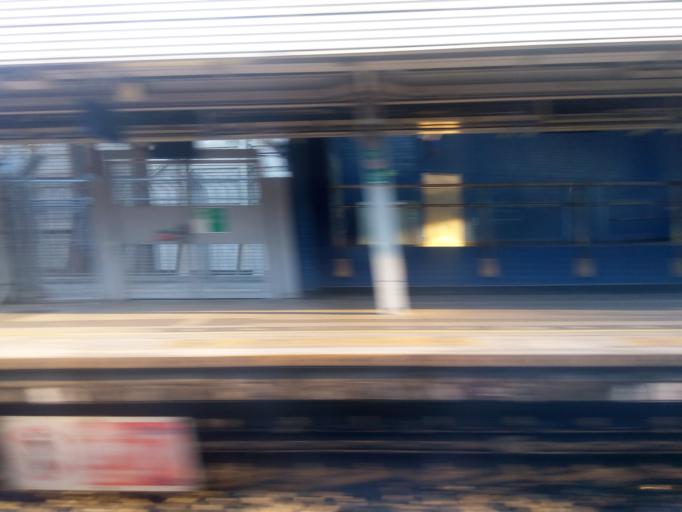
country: HK
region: Sha Tin
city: Sha Tin
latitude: 22.3736
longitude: 114.1792
